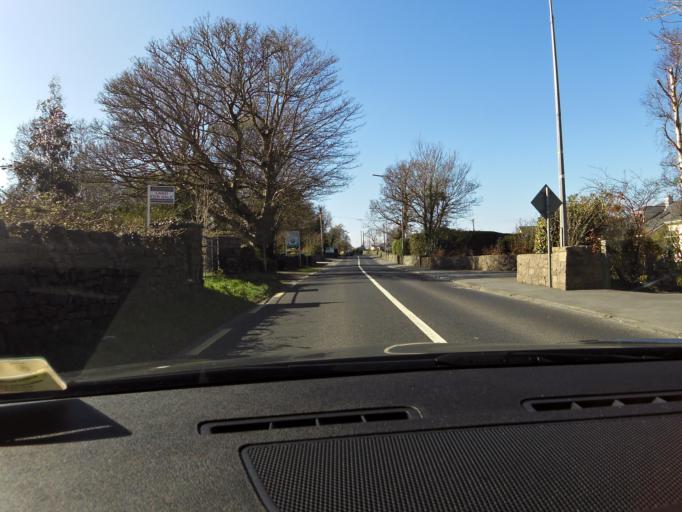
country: IE
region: Connaught
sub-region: County Galway
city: Oughterard
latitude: 53.4253
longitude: -9.3121
